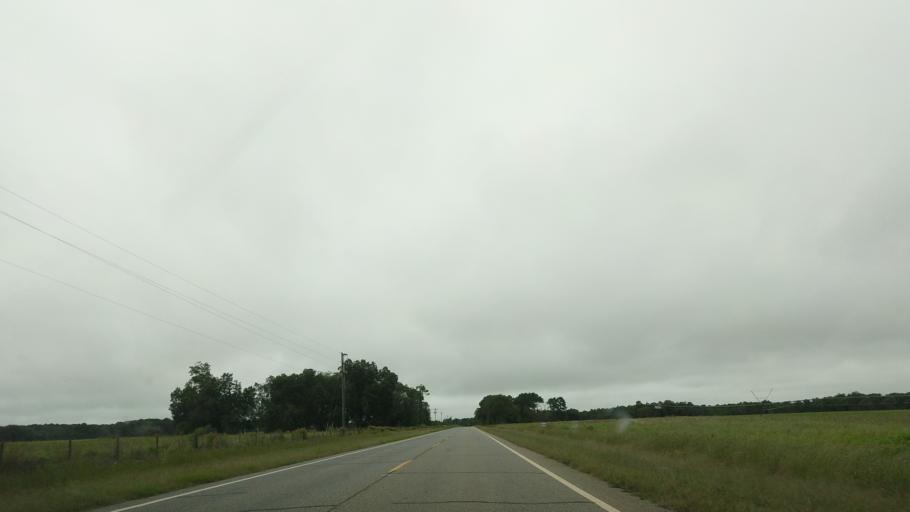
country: US
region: Georgia
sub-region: Irwin County
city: Ocilla
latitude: 31.5250
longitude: -83.2452
